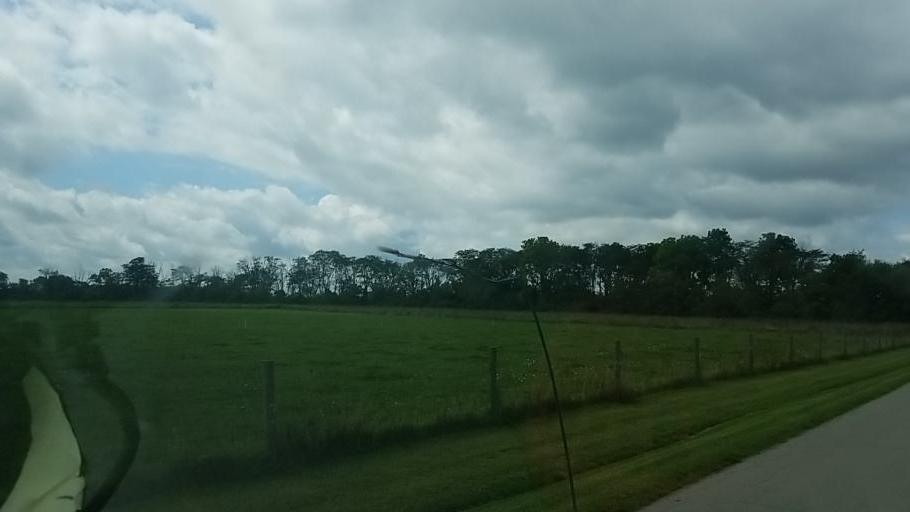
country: US
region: Ohio
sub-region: Madison County
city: Bethel
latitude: 39.6907
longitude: -83.4607
